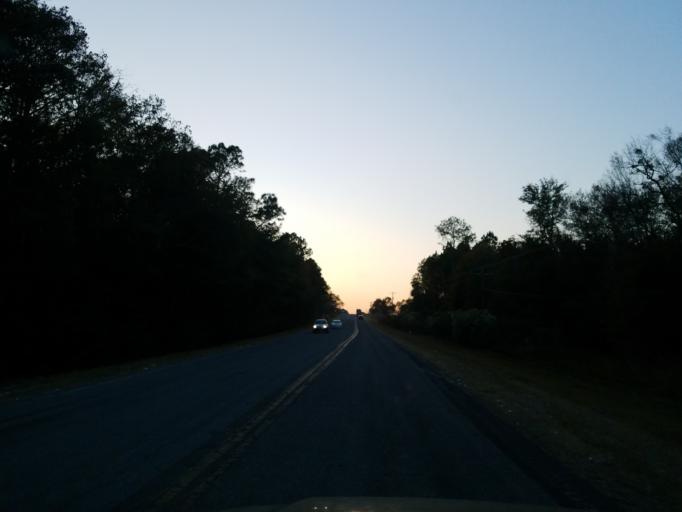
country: US
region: Georgia
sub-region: Ben Hill County
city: Fitzgerald
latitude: 31.7198
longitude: -83.3899
